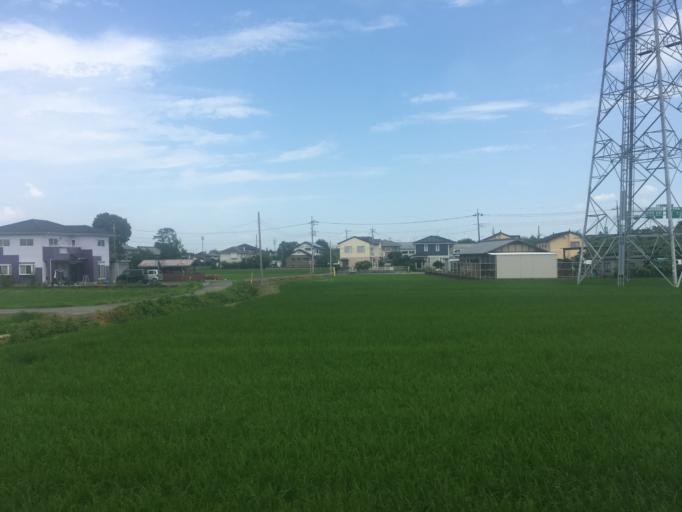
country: JP
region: Gunma
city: Fujioka
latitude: 36.2742
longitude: 139.0838
